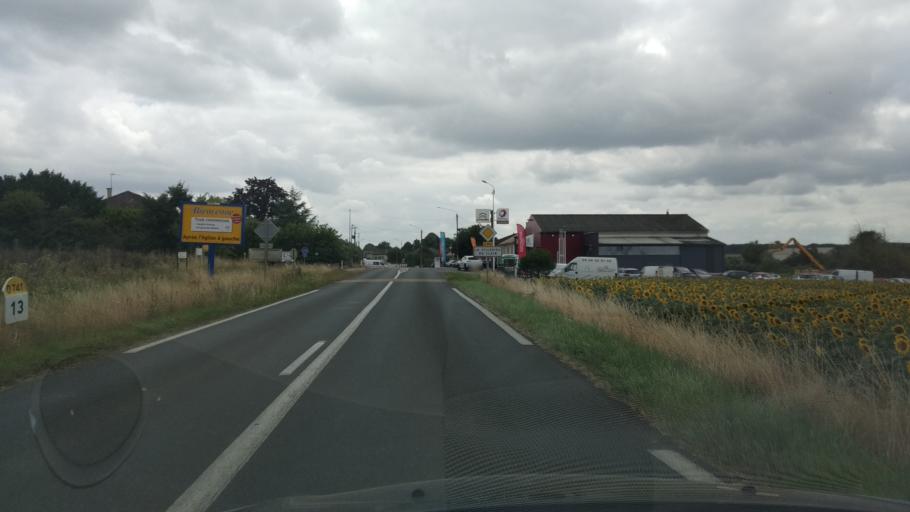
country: FR
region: Poitou-Charentes
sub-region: Departement de la Vienne
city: La Villedieu-du-Clain
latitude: 46.4623
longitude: 0.3671
